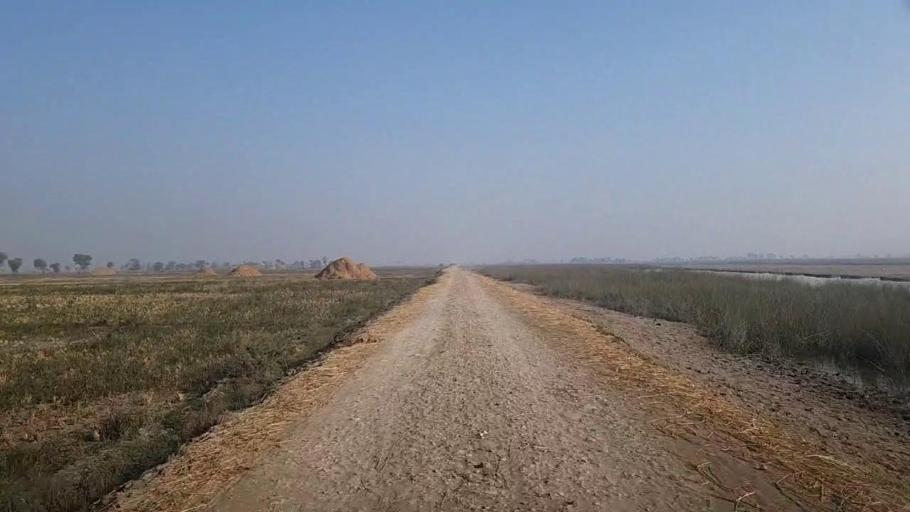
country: PK
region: Sindh
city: Radhan
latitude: 27.1380
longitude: 67.9064
